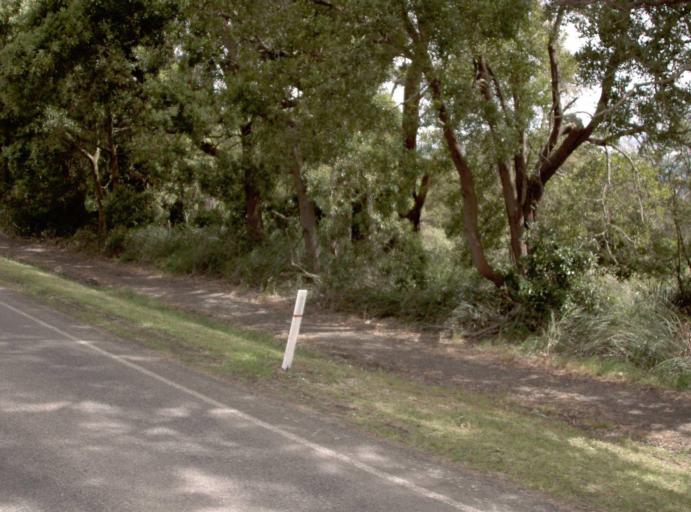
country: AU
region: Victoria
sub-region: Latrobe
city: Moe
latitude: -38.0784
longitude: 146.1862
